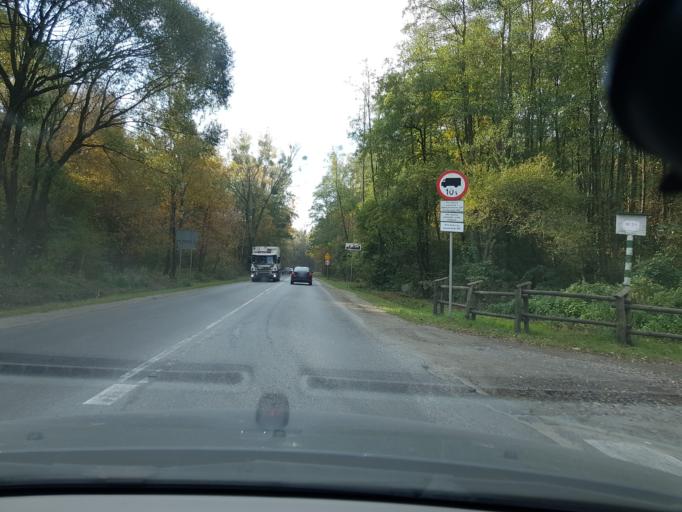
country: PL
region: Masovian Voivodeship
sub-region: Powiat warszawski zachodni
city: Babice
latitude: 52.2749
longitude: 20.8753
